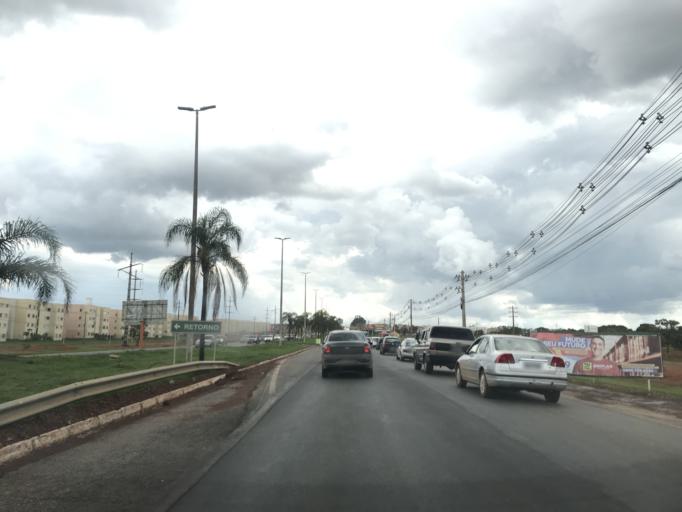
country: BR
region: Federal District
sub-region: Brasilia
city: Brasilia
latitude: -15.8930
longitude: -48.0570
